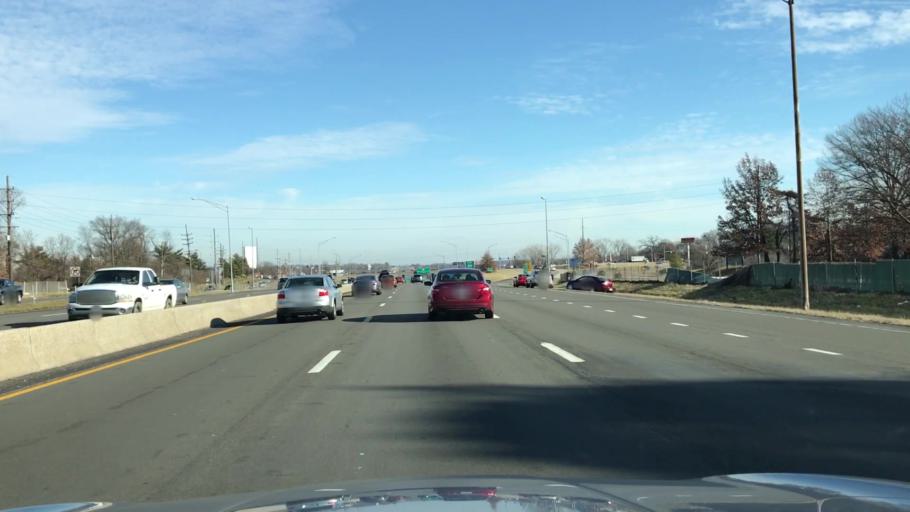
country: US
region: Missouri
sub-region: Saint Louis County
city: Dellwood
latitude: 38.7713
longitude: -90.2855
